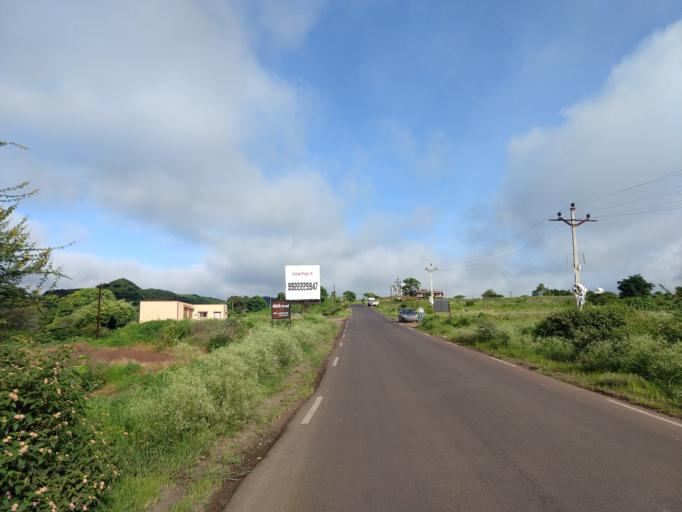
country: IN
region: Maharashtra
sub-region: Pune Division
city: Khed
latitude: 18.3943
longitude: 73.9182
